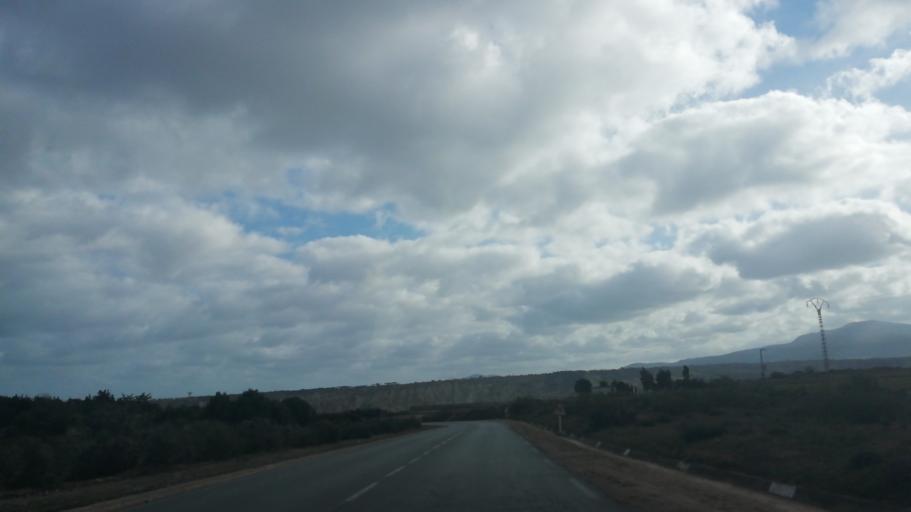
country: DZ
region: Relizane
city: Mazouna
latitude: 36.2917
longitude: 0.6533
